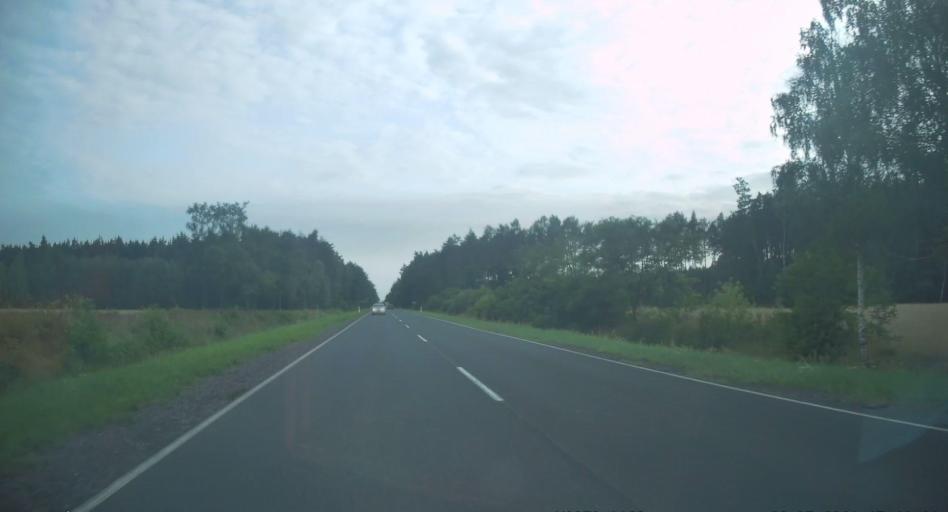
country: PL
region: Lodz Voivodeship
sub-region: Powiat radomszczanski
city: Plawno
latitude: 50.9887
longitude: 19.4137
